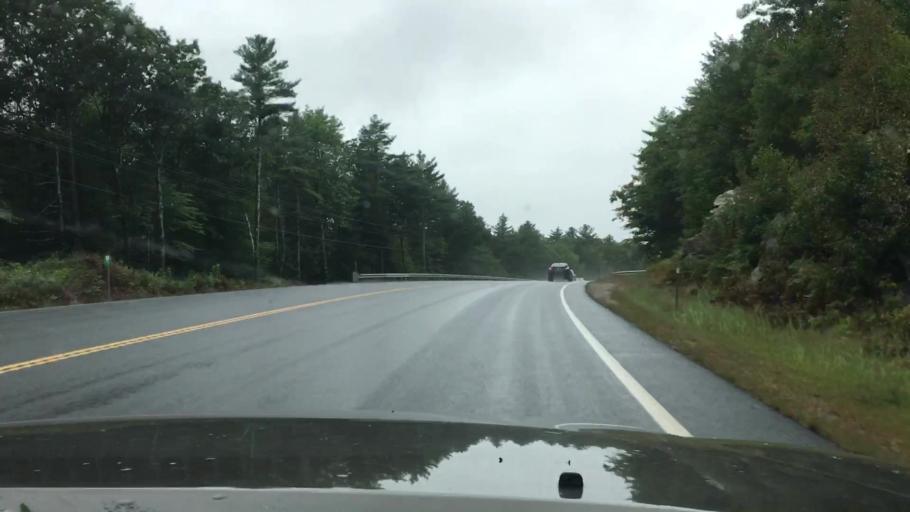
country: US
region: New Hampshire
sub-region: Cheshire County
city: Keene
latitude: 42.9678
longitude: -72.2478
